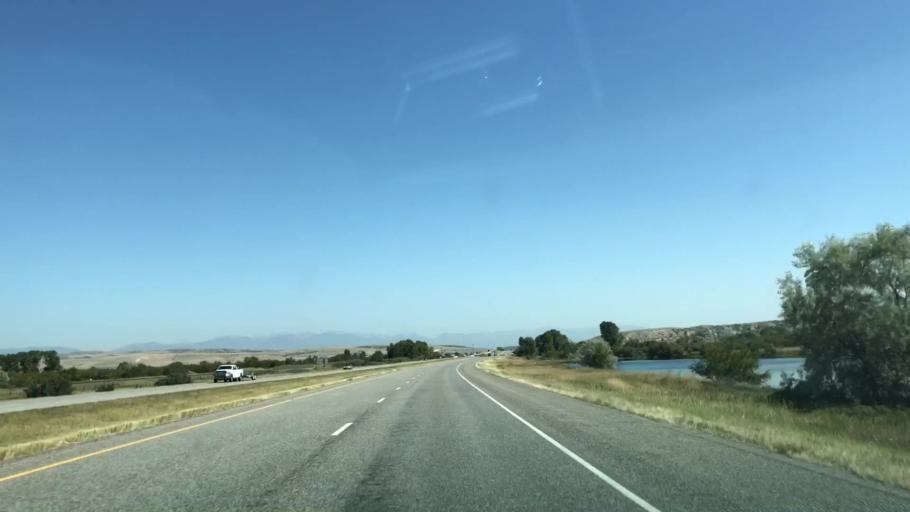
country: US
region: Montana
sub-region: Gallatin County
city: Three Forks
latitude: 45.8983
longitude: -111.5074
